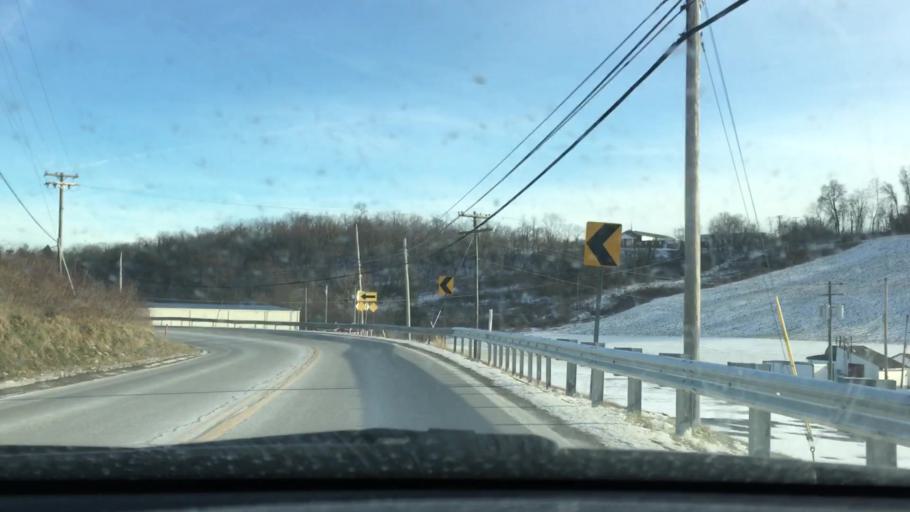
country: US
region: Pennsylvania
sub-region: Washington County
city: Gastonville
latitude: 40.2709
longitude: -80.0198
